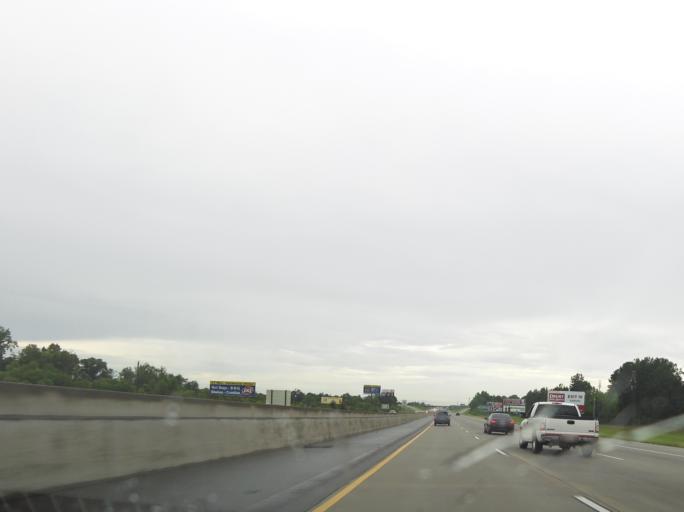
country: US
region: Georgia
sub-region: Cook County
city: Adel
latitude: 31.1209
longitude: -83.4323
